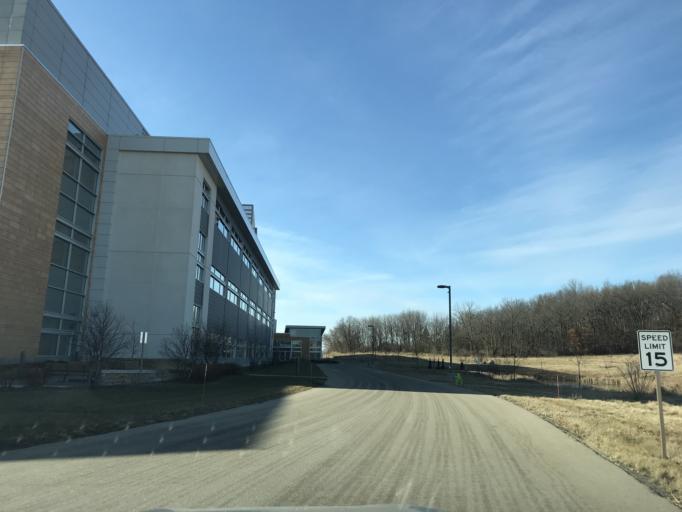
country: US
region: Wisconsin
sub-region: Dane County
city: Windsor
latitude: 43.1557
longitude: -89.3000
